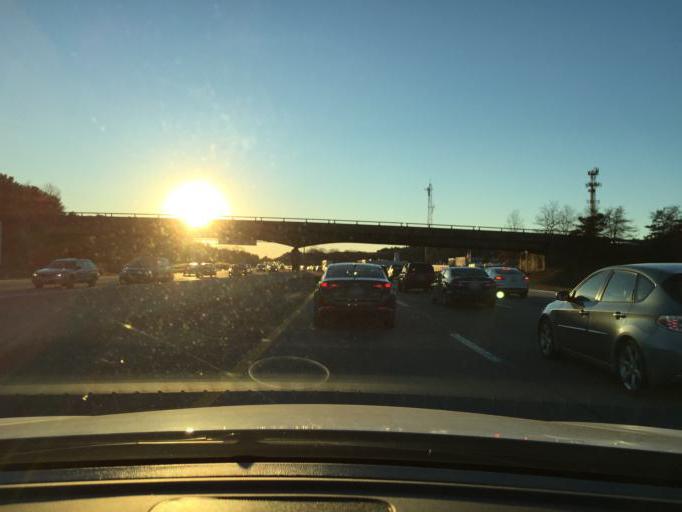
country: US
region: Massachusetts
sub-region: Middlesex County
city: Weston
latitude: 42.3342
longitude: -71.3165
